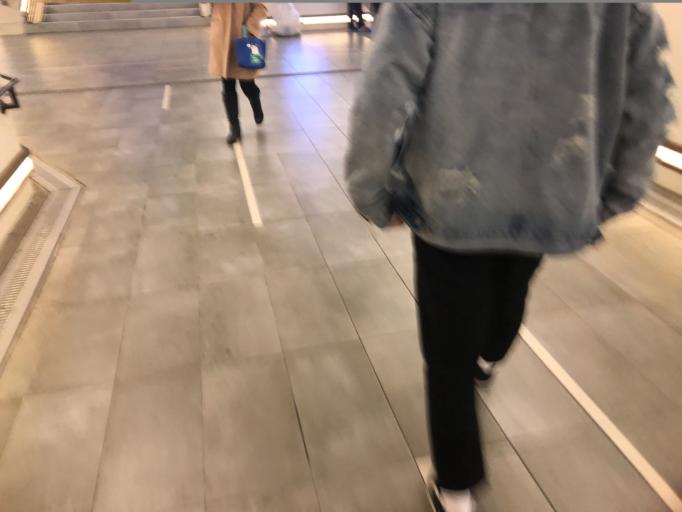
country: TW
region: Taiwan
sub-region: Hsinchu
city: Hsinchu
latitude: 24.8013
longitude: 120.9729
